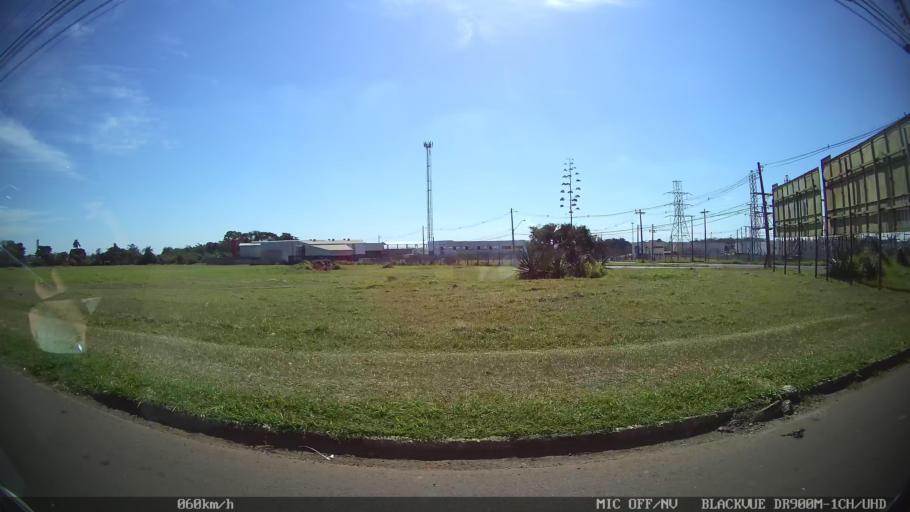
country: BR
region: Sao Paulo
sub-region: Franca
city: Franca
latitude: -20.5469
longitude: -47.4344
